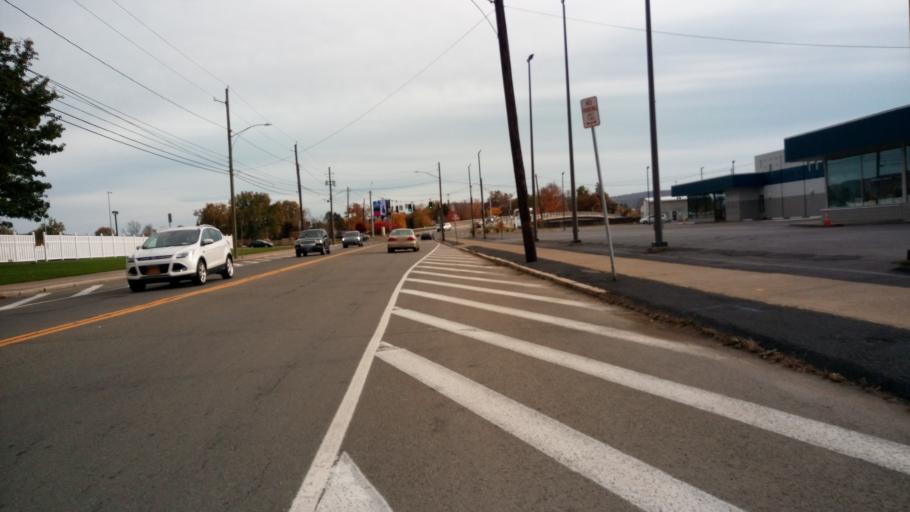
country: US
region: New York
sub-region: Chemung County
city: Elmira
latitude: 42.0897
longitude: -76.7984
